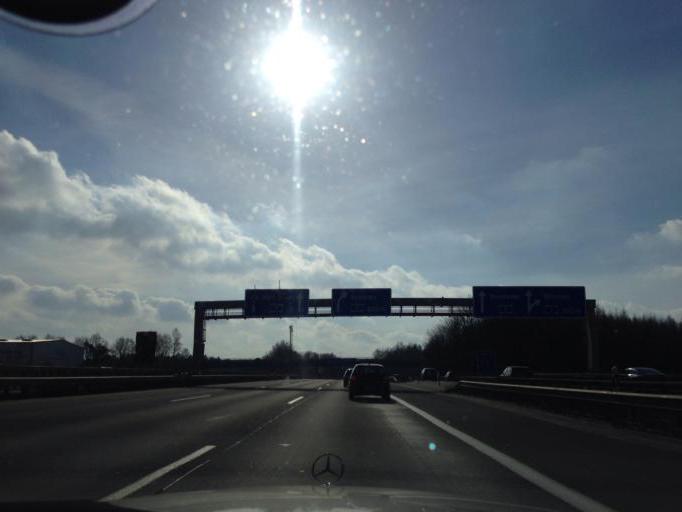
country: DE
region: Lower Saxony
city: Harmstorf
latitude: 53.3885
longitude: 10.0213
